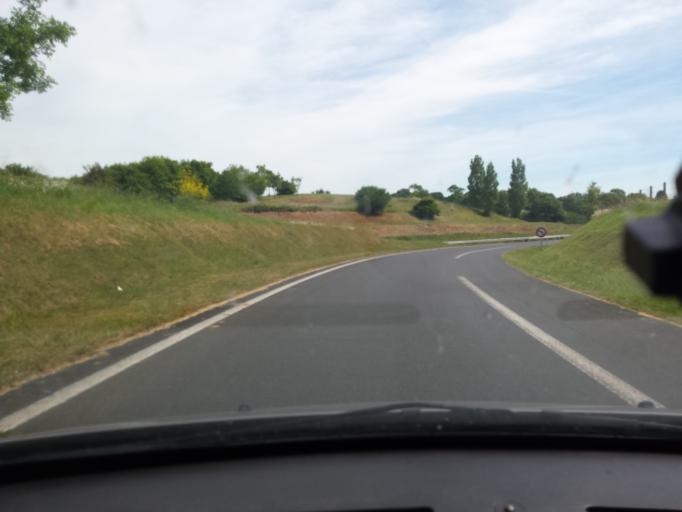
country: FR
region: Lower Normandy
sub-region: Departement du Calvados
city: Grandcamp-Maisy
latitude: 49.3380
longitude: -1.0069
